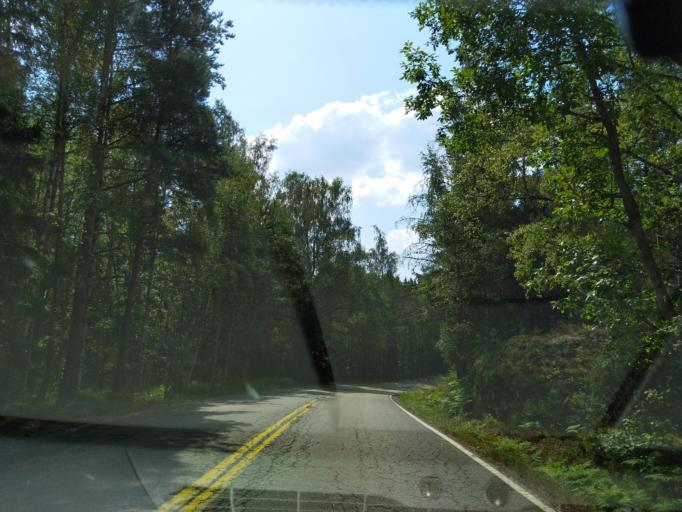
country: FI
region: Uusimaa
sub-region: Helsinki
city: Kirkkonummi
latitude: 60.0325
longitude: 24.4858
